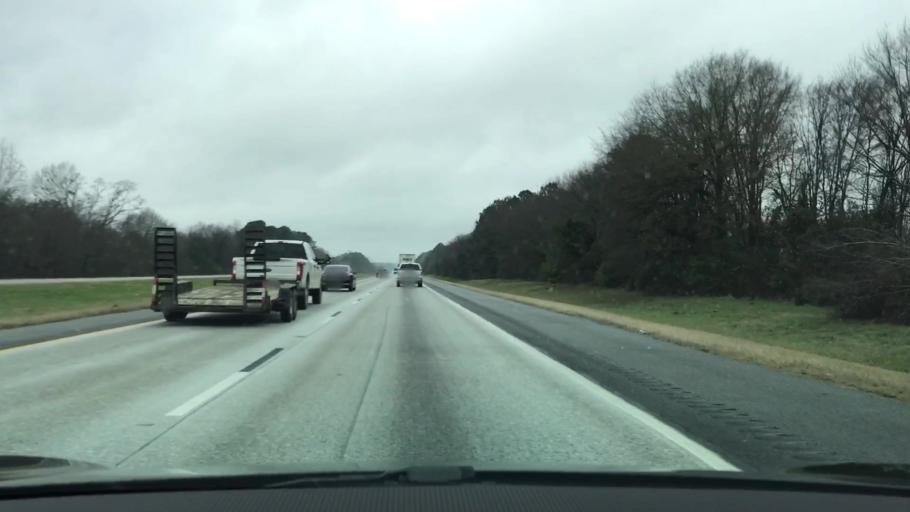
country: US
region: Georgia
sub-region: Putnam County
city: Jefferson
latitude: 33.5411
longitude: -83.3210
